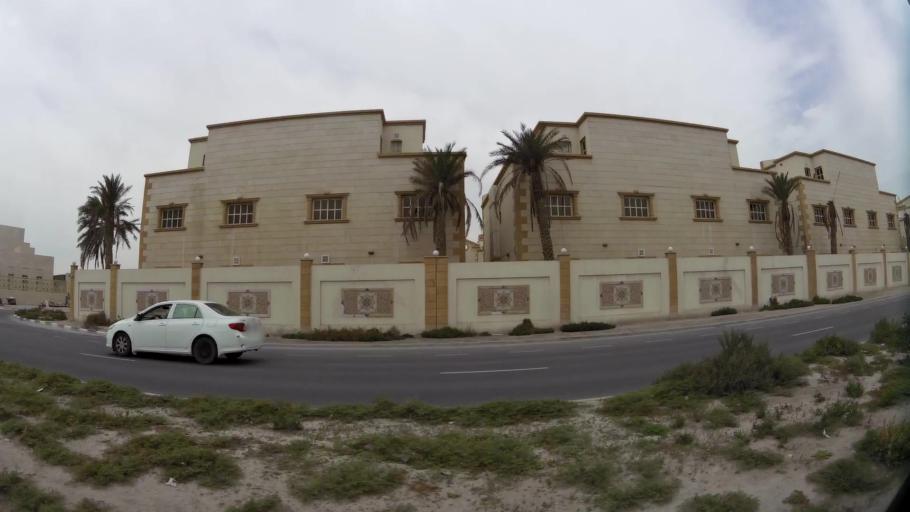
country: QA
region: Baladiyat ar Rayyan
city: Ar Rayyan
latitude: 25.2283
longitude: 51.4611
